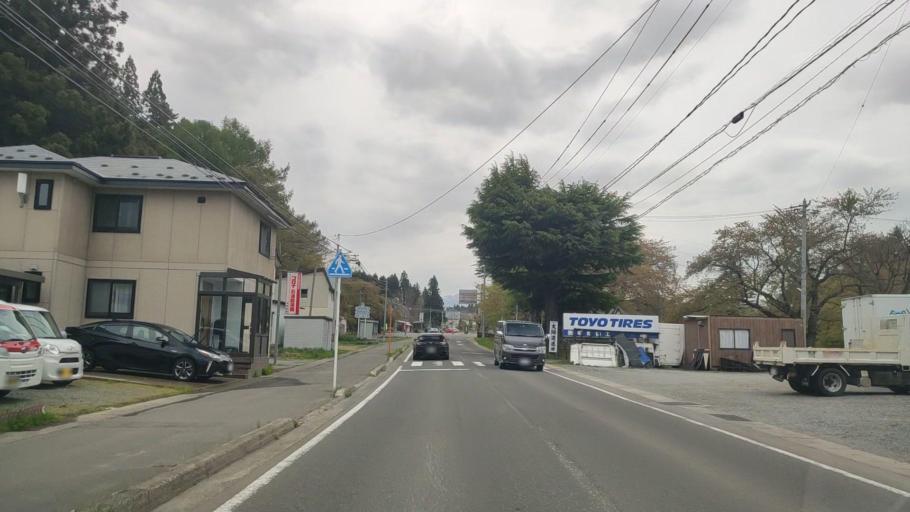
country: JP
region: Aomori
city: Aomori Shi
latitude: 40.7866
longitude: 140.7888
